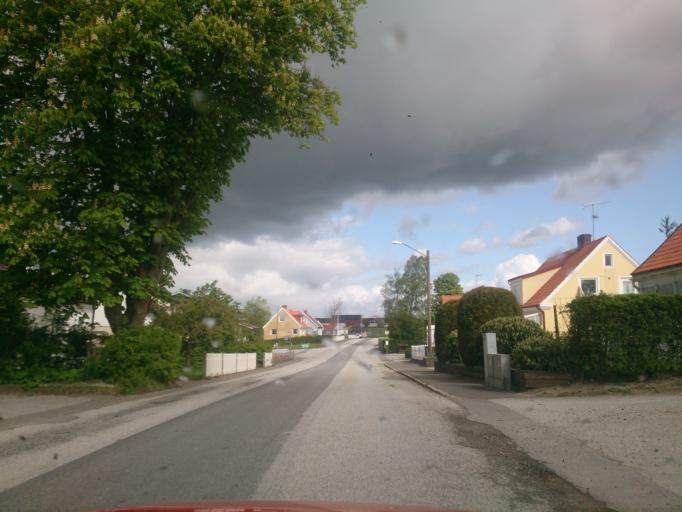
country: SE
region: Skane
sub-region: Ystads Kommun
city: Ystad
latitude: 55.4881
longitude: 13.7128
